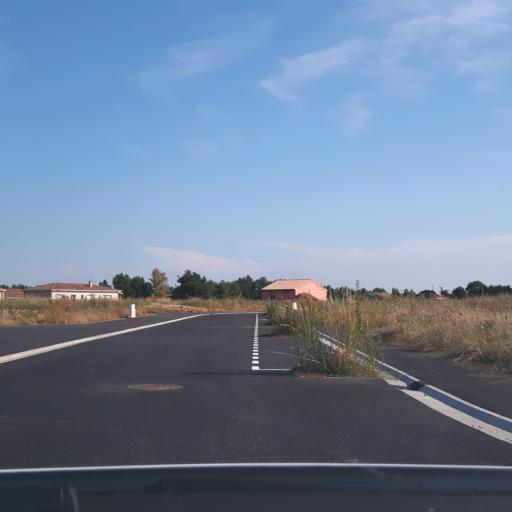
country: FR
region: Midi-Pyrenees
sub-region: Departement de la Haute-Garonne
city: Fronton
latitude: 43.8342
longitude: 1.3973
